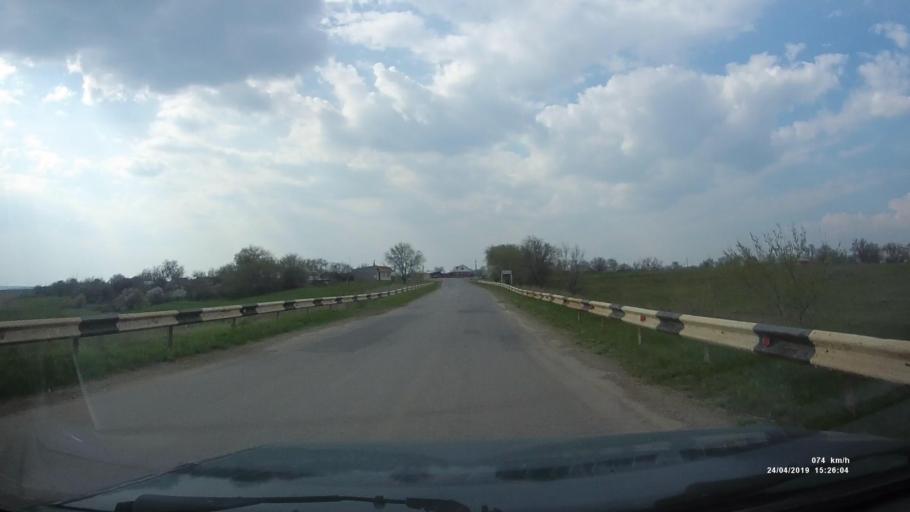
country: RU
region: Rostov
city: Remontnoye
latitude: 46.5561
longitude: 43.0377
